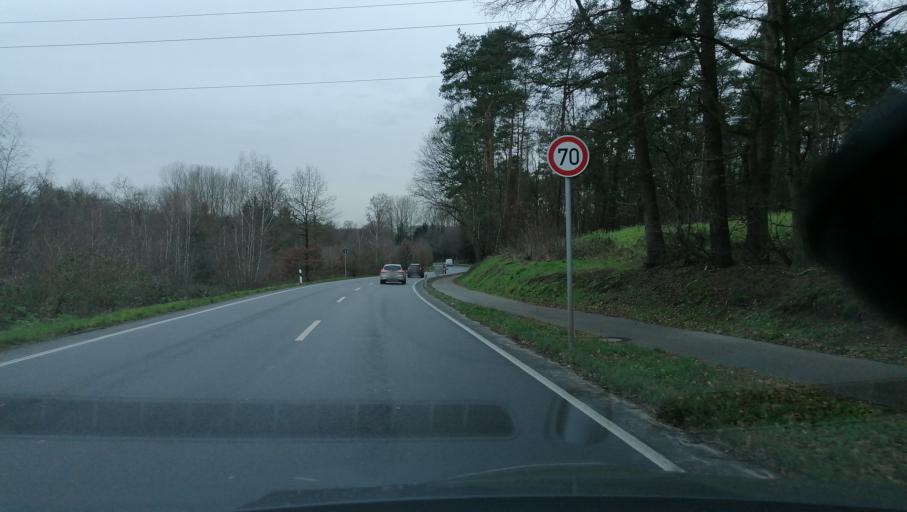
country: DE
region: North Rhine-Westphalia
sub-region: Regierungsbezirk Munster
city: Klein Reken
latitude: 51.8048
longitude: 7.0353
